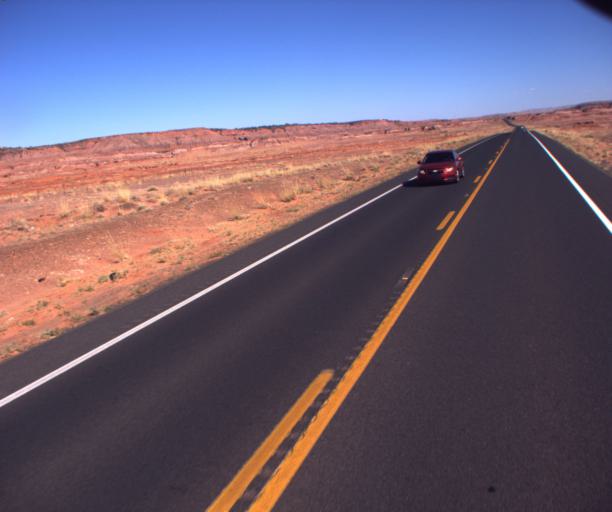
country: US
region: Arizona
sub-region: Coconino County
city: Tuba City
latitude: 36.1013
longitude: -111.3051
